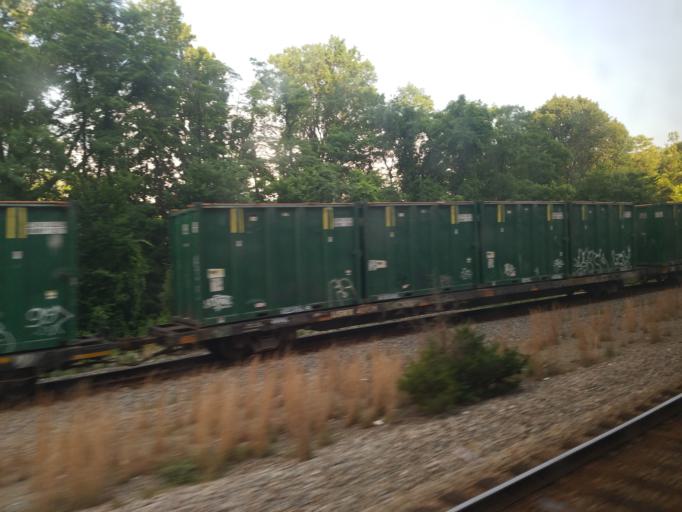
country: US
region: Washington, D.C.
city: Washington, D.C.
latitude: 38.8530
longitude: -77.0482
